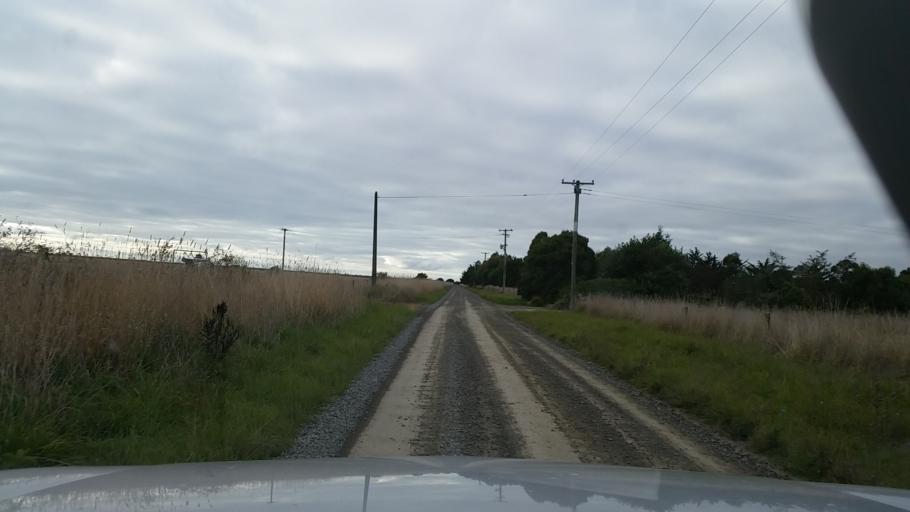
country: NZ
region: Marlborough
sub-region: Marlborough District
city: Blenheim
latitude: -41.5117
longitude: 174.0391
